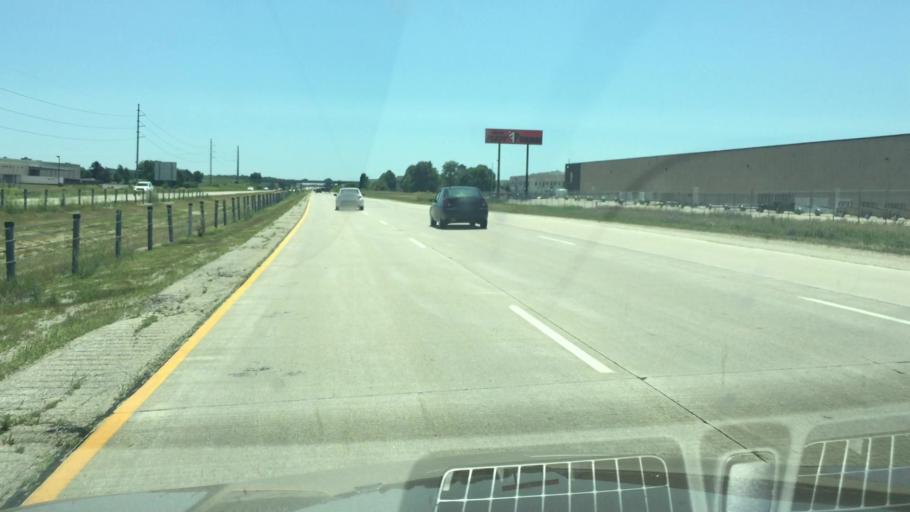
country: US
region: Wisconsin
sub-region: Dodge County
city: Beaver Dam
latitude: 43.4827
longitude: -88.8155
